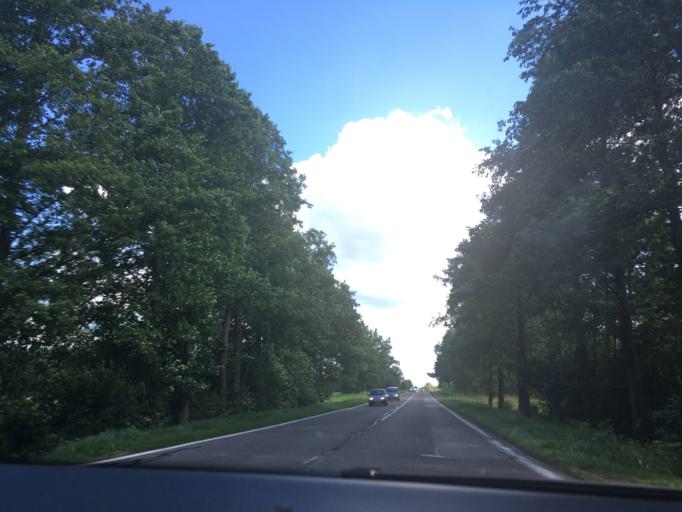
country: PL
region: Podlasie
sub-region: Powiat bialostocki
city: Dobrzyniewo Duze
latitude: 53.3336
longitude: 23.1100
